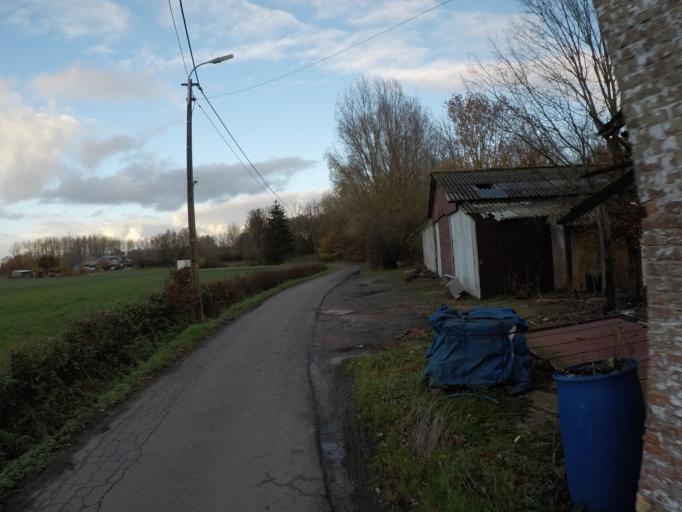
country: BE
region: Flanders
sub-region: Provincie Vlaams-Brabant
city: Londerzeel
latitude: 51.0164
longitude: 4.2983
